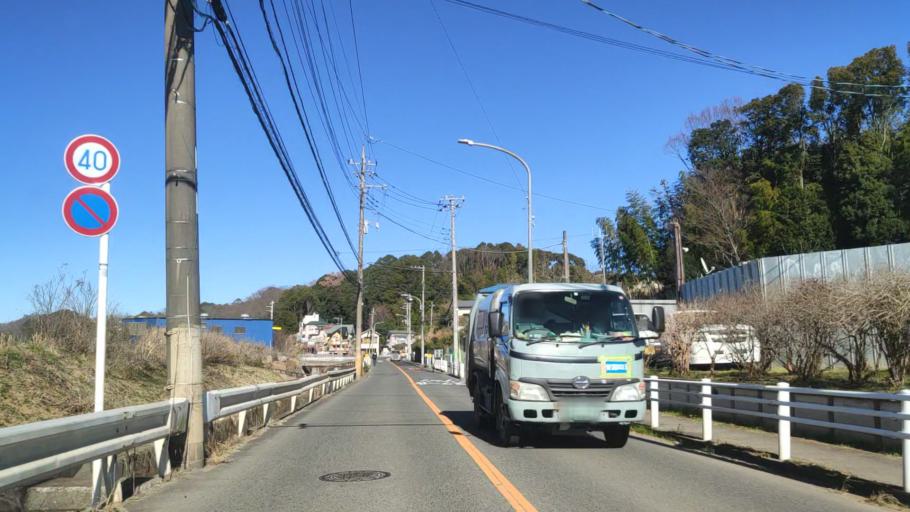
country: JP
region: Kanagawa
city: Minami-rinkan
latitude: 35.5089
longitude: 139.5200
